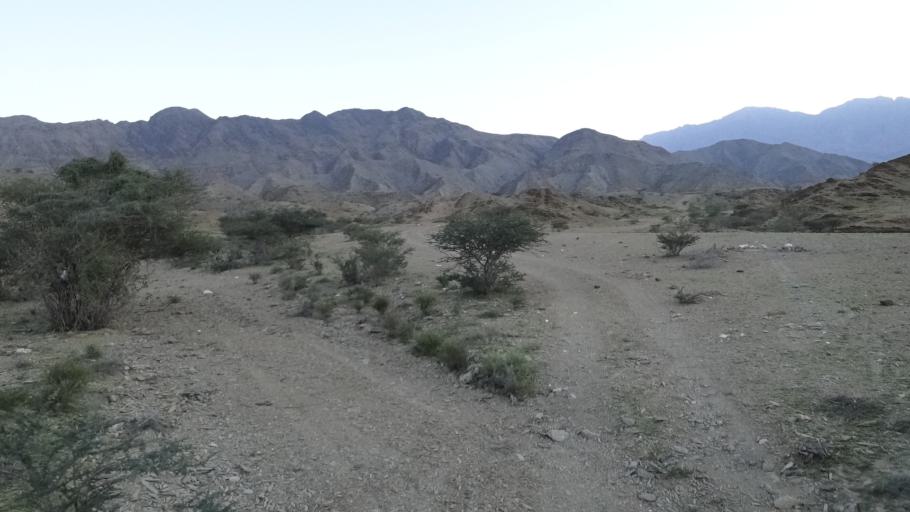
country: OM
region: Al Batinah
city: Rustaq
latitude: 23.2735
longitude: 57.3608
